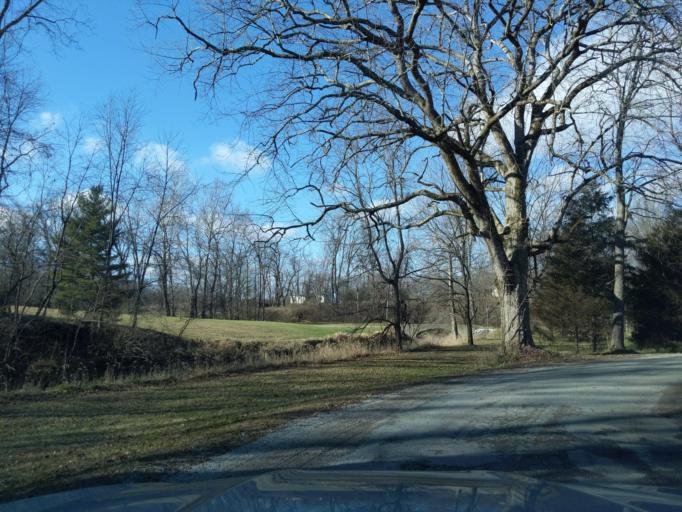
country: US
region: Indiana
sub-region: Decatur County
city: Greensburg
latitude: 39.2414
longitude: -85.4627
